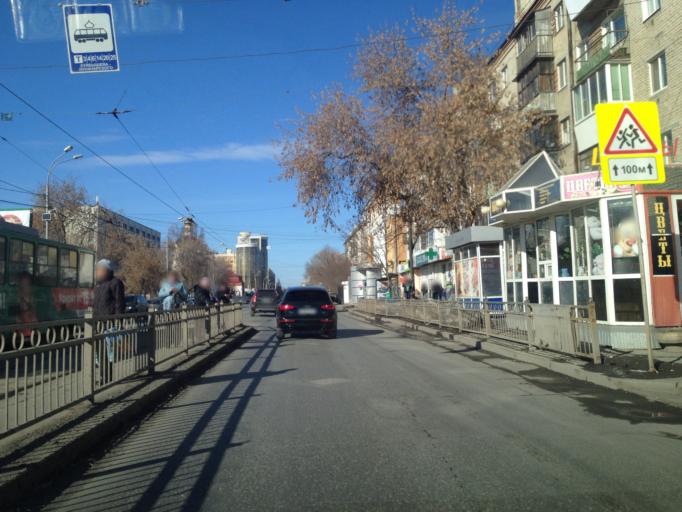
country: RU
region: Sverdlovsk
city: Yekaterinburg
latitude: 56.8299
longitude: 60.6244
